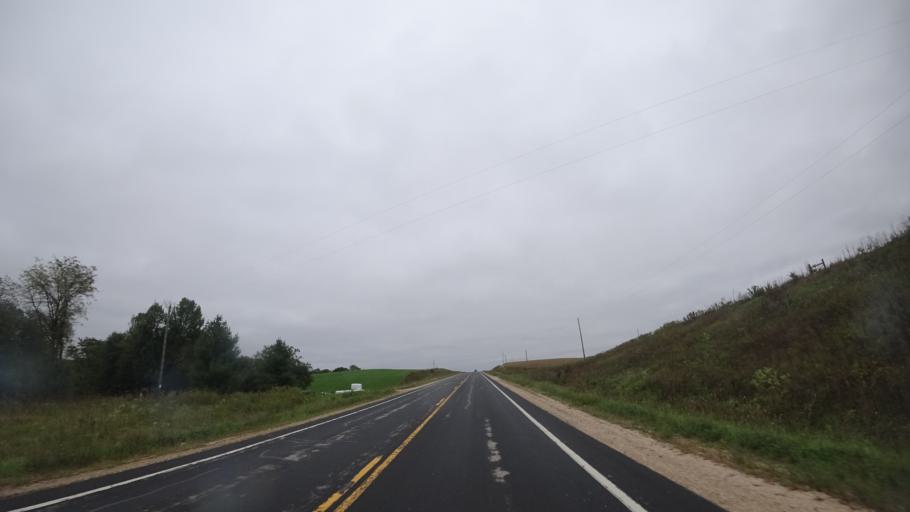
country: US
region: Wisconsin
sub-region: Grant County
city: Boscobel
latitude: 43.1083
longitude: -90.8071
